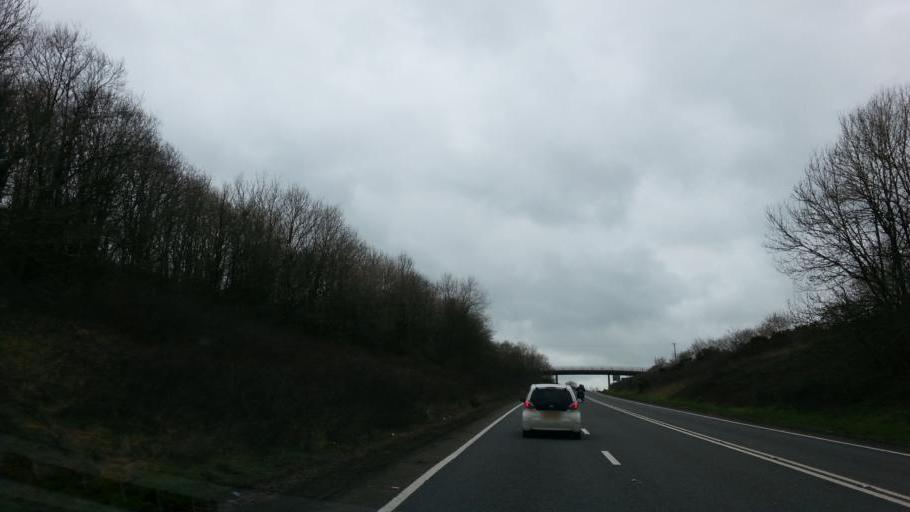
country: GB
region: England
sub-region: Devon
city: South Molton
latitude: 51.0022
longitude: -3.7431
